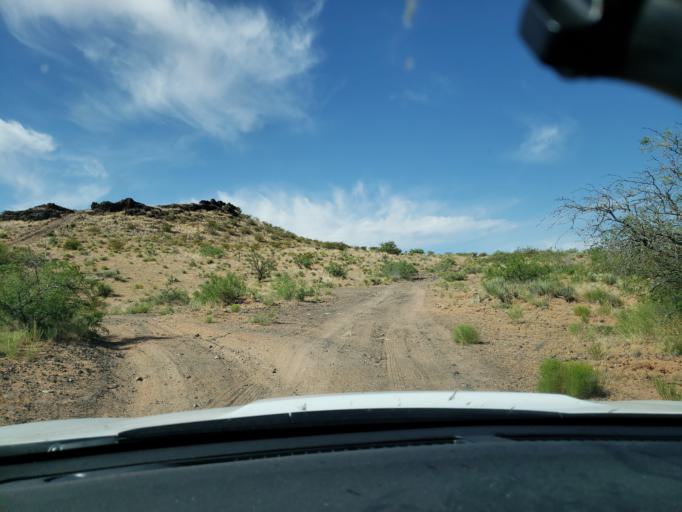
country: US
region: New Mexico
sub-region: Dona Ana County
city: San Miguel
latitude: 32.0793
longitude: -106.7933
